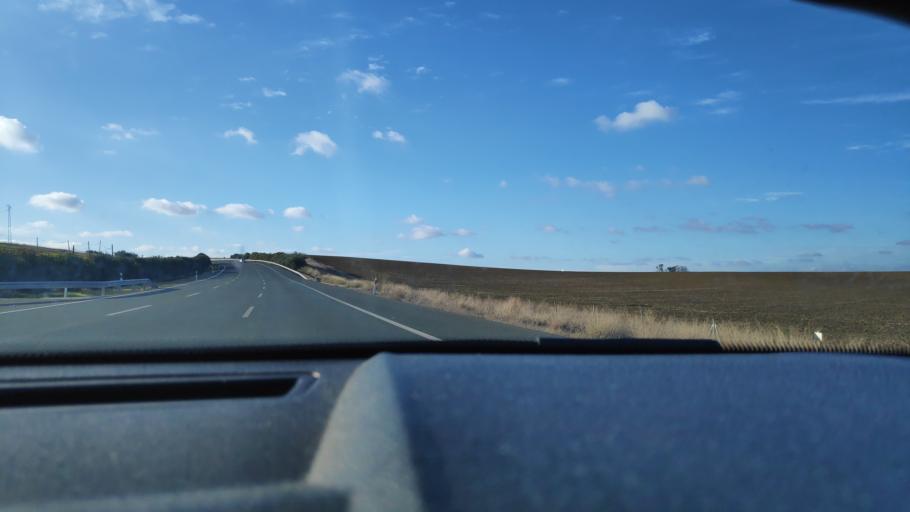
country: ES
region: Andalusia
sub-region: Provincia de Sevilla
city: La Luisiana
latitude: 37.5281
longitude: -5.2916
